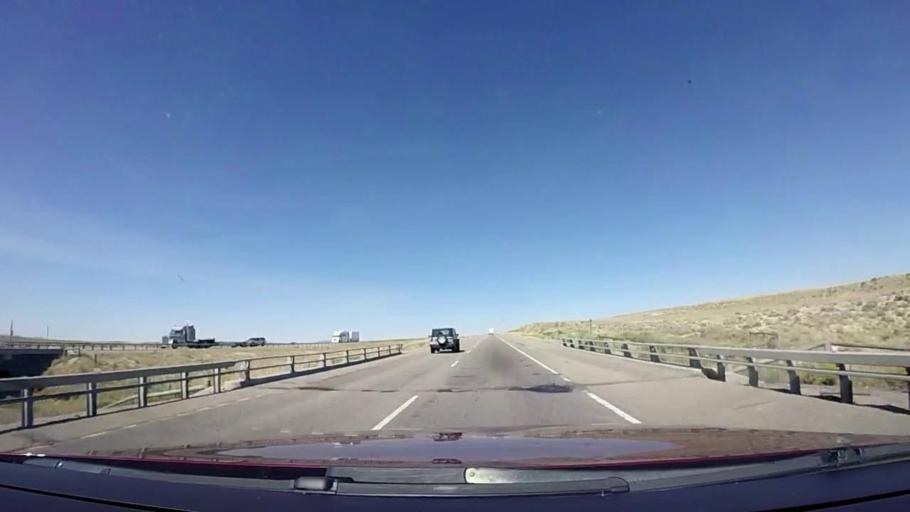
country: US
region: Wyoming
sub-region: Sweetwater County
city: Rock Springs
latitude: 41.6391
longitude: -108.4671
